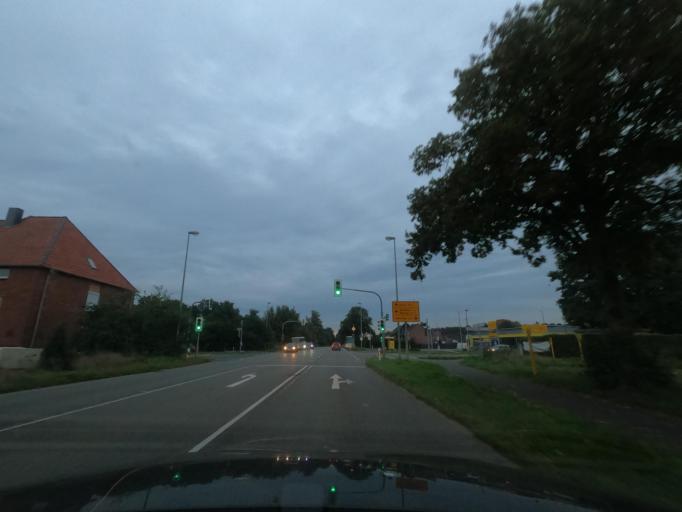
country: DE
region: North Rhine-Westphalia
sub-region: Regierungsbezirk Dusseldorf
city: Mehrhoog
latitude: 51.7365
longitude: 6.4996
